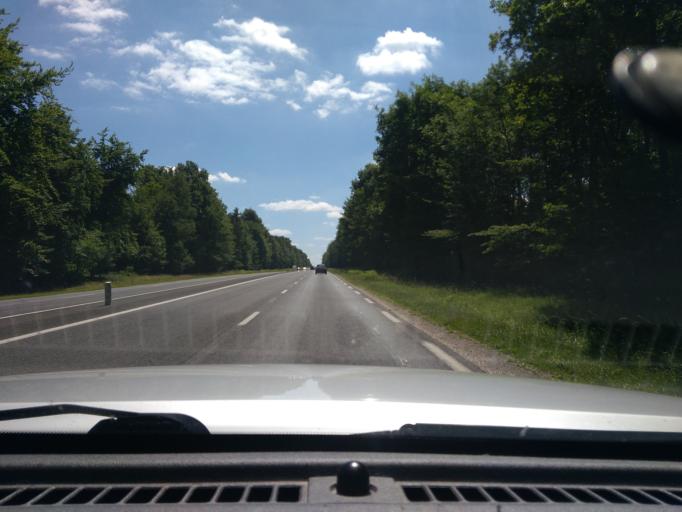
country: FR
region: Ile-de-France
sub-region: Departement de Seine-et-Marne
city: Thomery
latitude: 48.3876
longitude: 2.7606
